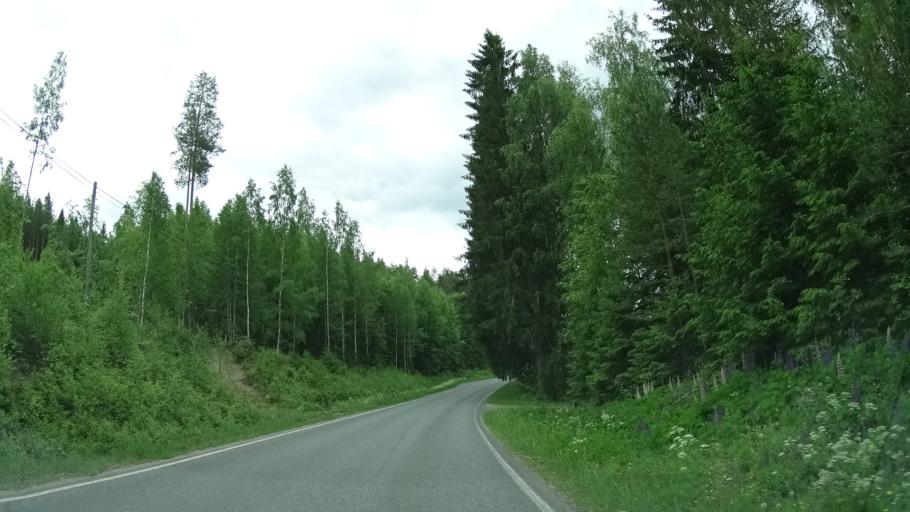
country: FI
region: Central Finland
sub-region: Jyvaeskylae
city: Toivakka
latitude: 62.0560
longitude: 26.0285
